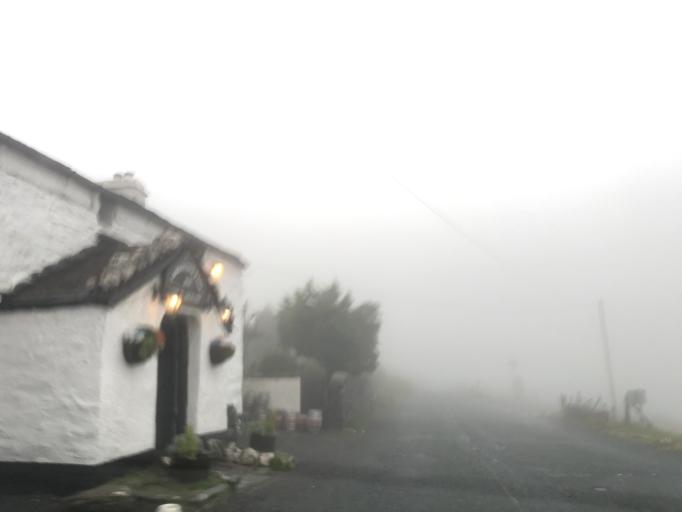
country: GB
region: England
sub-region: Cumbria
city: Ambleside
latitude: 54.4644
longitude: -2.9253
